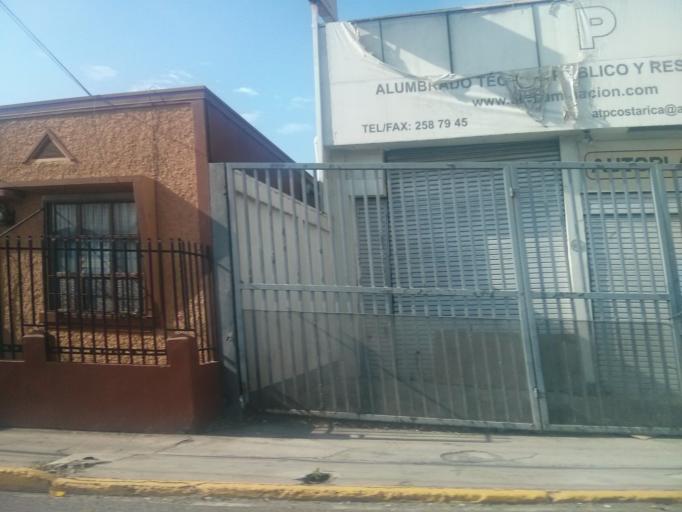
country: CR
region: San Jose
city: Colima
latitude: 9.9476
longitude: -84.0859
